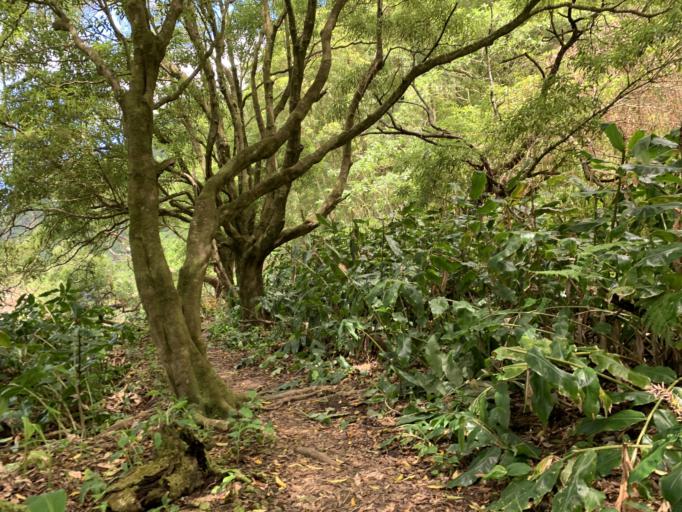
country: PT
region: Azores
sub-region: Ponta Delgada
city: Arrifes
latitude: 37.8417
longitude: -25.7877
